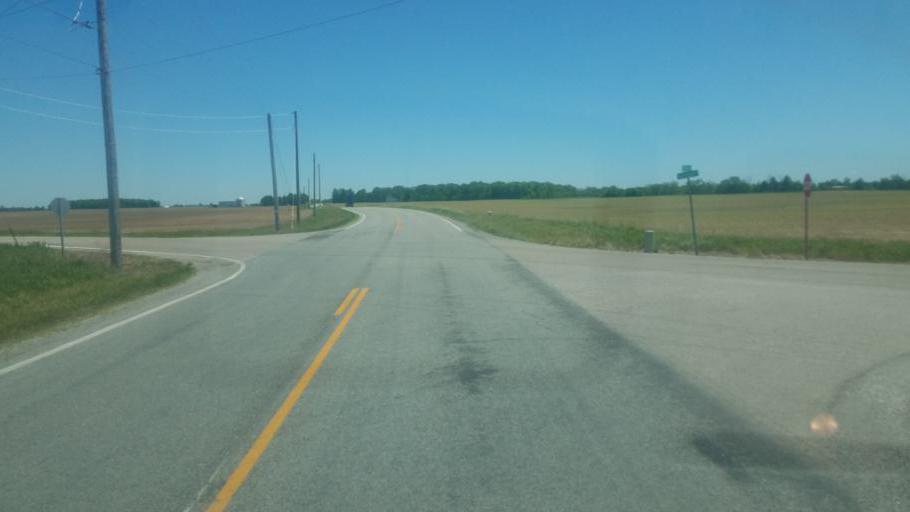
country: US
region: Ohio
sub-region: Miami County
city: Piqua
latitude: 40.2130
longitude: -84.3058
